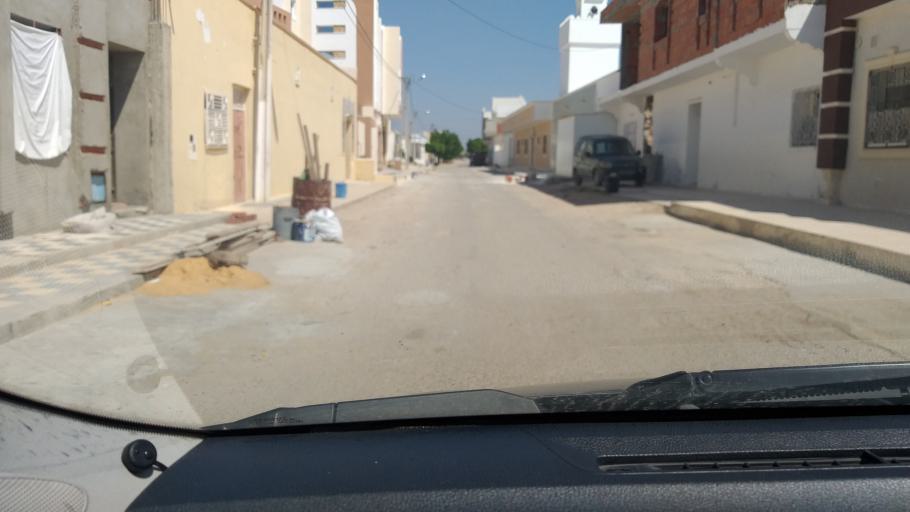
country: TN
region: Al Mahdiyah
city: El Jem
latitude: 35.2914
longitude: 10.7159
